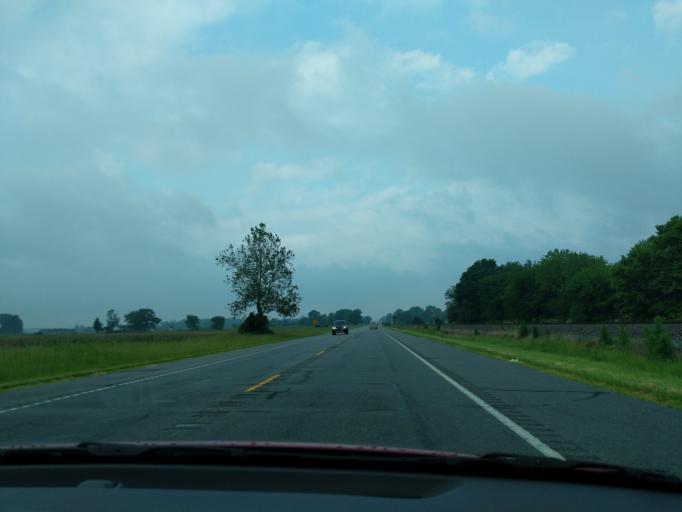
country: US
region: Indiana
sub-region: Hancock County
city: Fortville
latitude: 39.9178
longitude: -85.8786
